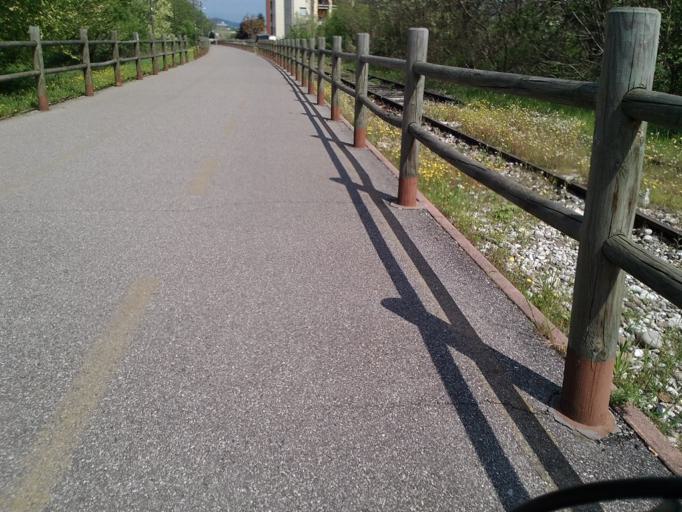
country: IT
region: Veneto
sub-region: Provincia di Verona
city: Verona
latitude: 45.4204
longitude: 10.9605
